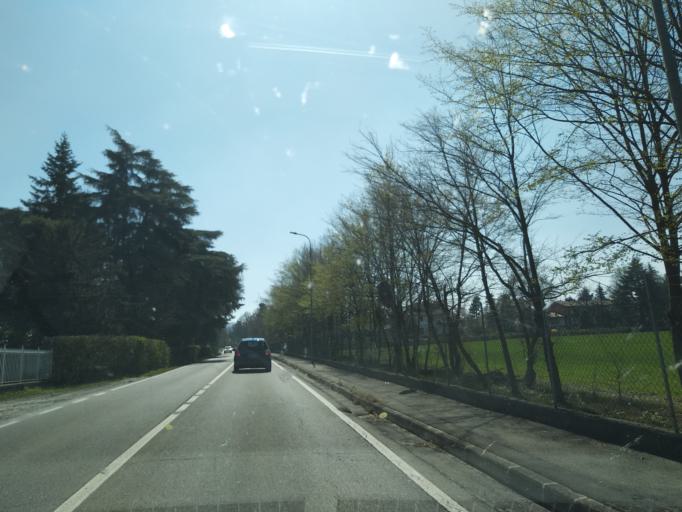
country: IT
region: Emilia-Romagna
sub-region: Provincia di Reggio Emilia
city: Albinea
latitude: 44.6295
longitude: 10.6059
